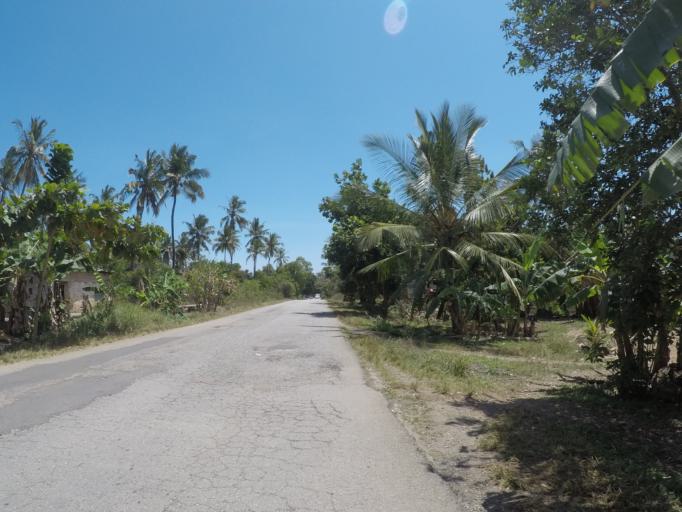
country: TZ
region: Zanzibar Central/South
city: Nganane
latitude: -6.2884
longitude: 39.4406
